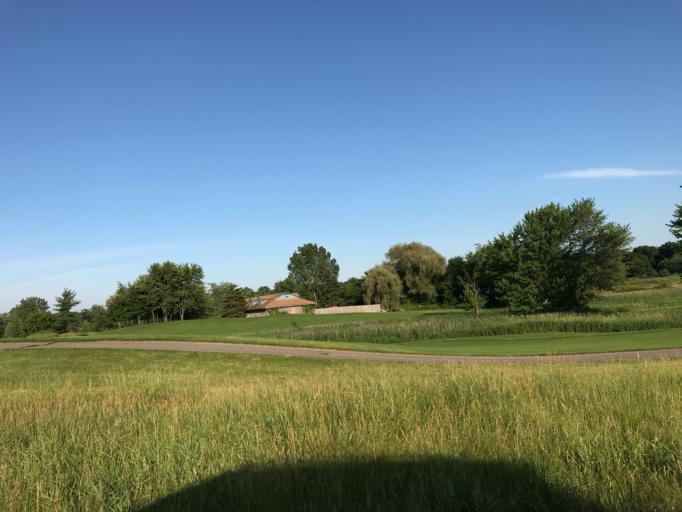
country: US
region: Michigan
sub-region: Oakland County
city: South Lyon
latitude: 42.4453
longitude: -83.6190
